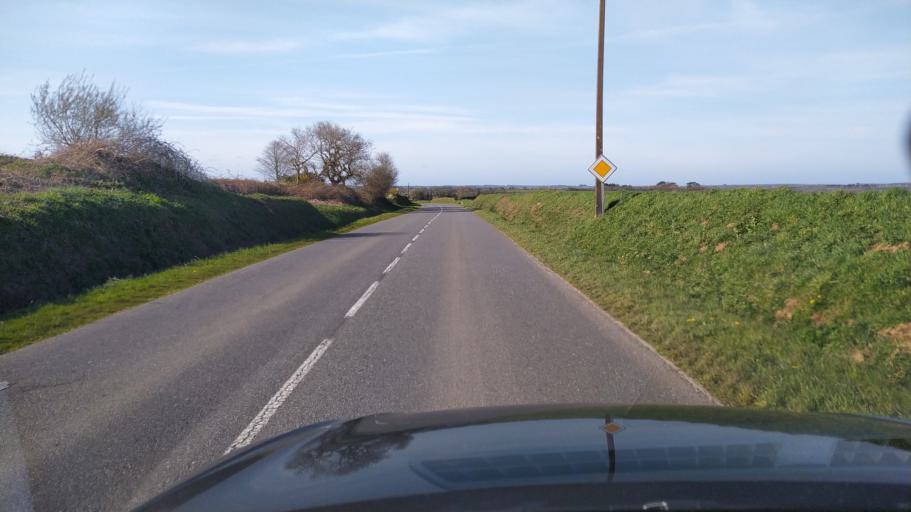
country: FR
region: Brittany
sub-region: Departement du Finistere
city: Lampaul-Guimiliau
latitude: 48.4669
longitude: -4.0186
